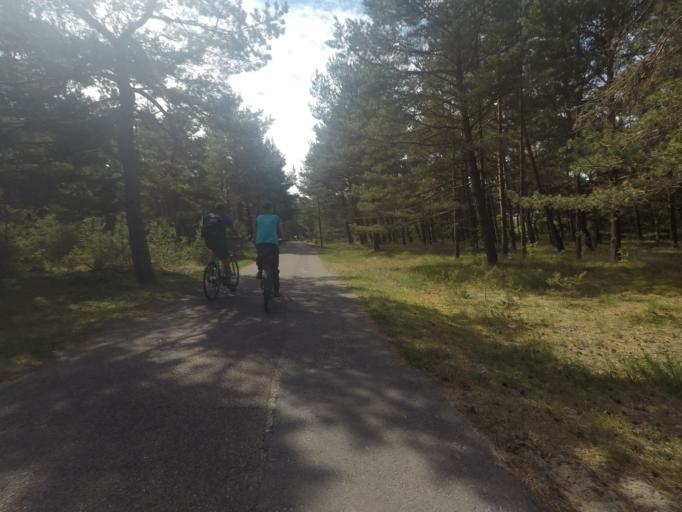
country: LT
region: Klaipedos apskritis
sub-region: Klaipeda
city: Klaipeda
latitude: 55.5476
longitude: 21.1012
